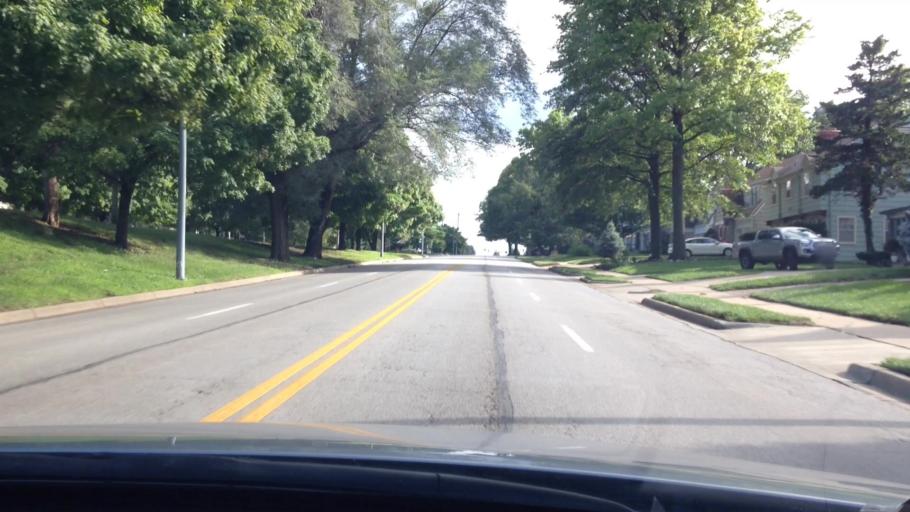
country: US
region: Kansas
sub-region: Johnson County
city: Mission Hills
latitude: 39.0032
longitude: -94.5936
